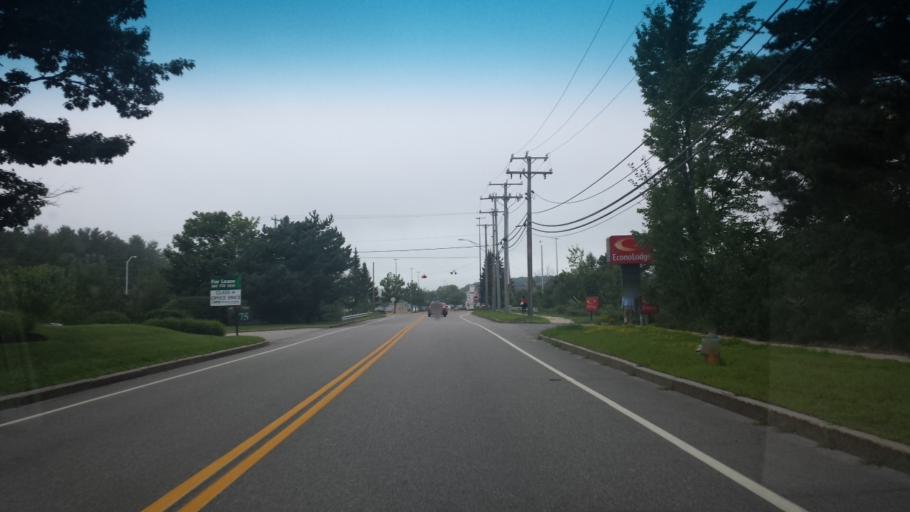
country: US
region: Maine
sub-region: Cumberland County
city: South Portland Gardens
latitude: 43.6302
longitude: -70.3297
